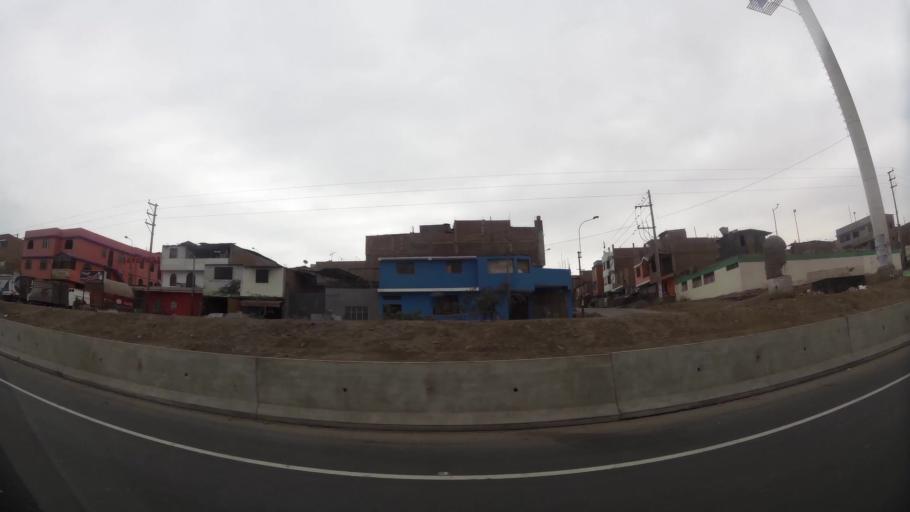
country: PE
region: Lima
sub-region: Lima
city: Surco
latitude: -12.1956
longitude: -76.9730
